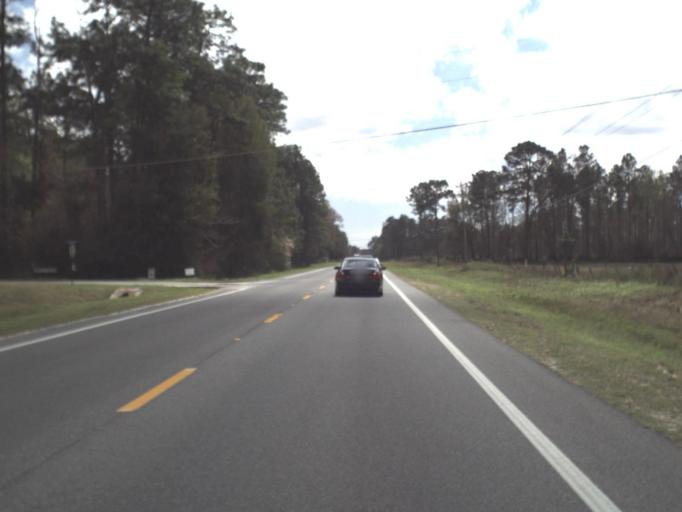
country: US
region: Florida
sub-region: Wakulla County
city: Crawfordville
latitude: 30.2328
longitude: -84.3624
